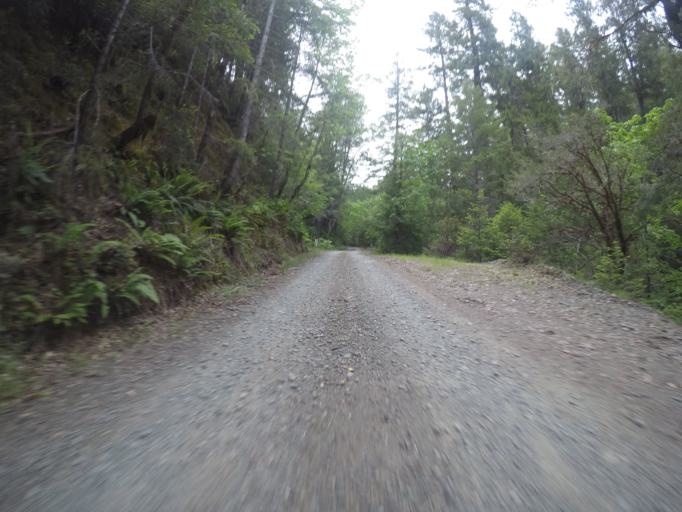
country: US
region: California
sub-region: Del Norte County
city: Bertsch-Oceanview
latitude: 41.7402
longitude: -123.8793
